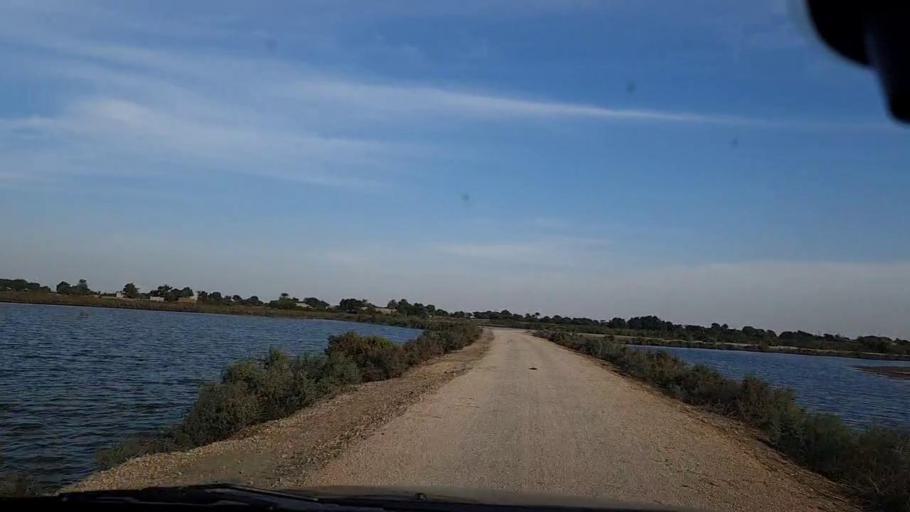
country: PK
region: Sindh
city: Mirpur Batoro
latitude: 24.6544
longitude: 68.2918
